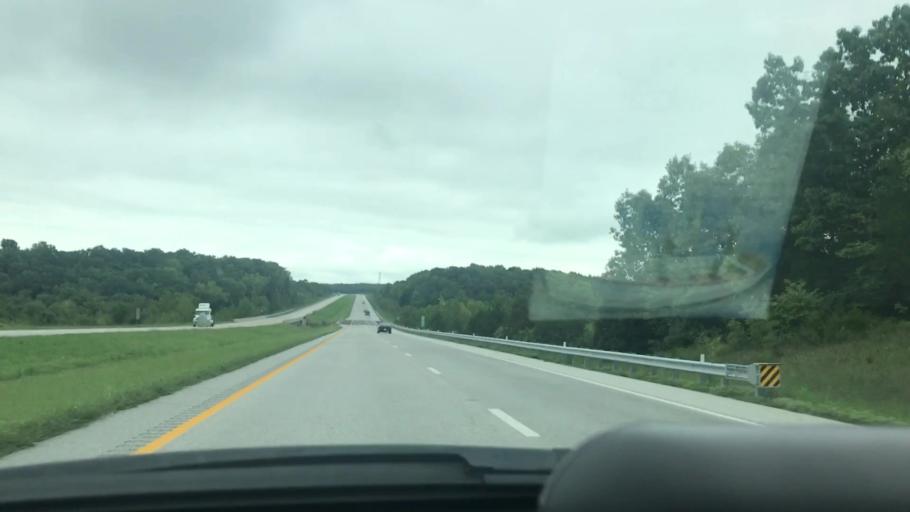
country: US
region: Missouri
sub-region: Greene County
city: Strafford
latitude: 37.3080
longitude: -93.1736
